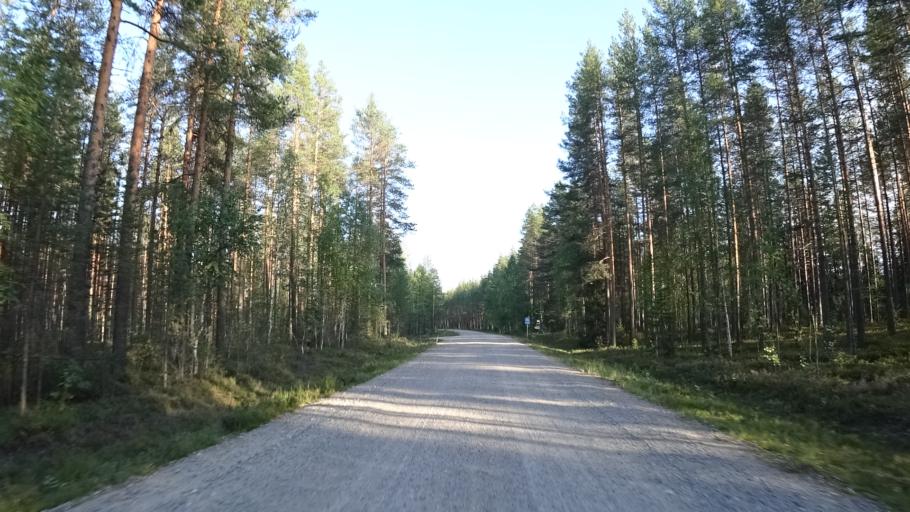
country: FI
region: North Karelia
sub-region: Joensuu
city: Ilomantsi
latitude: 63.1298
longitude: 30.7121
